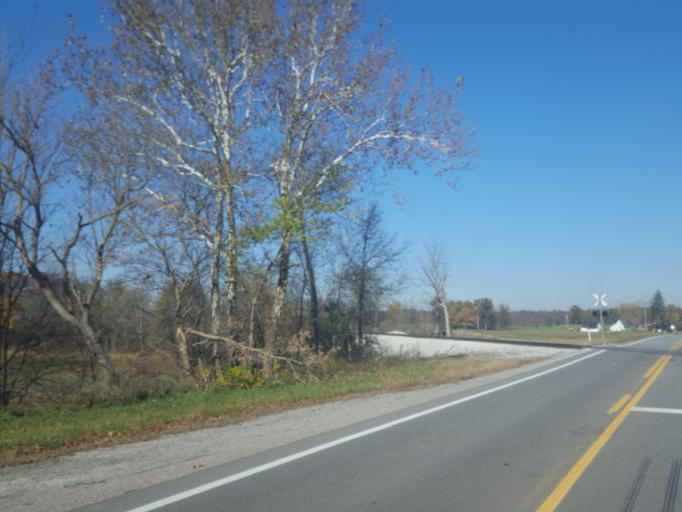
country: US
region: Ohio
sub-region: Wyandot County
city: Carey
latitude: 40.9596
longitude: -83.2731
